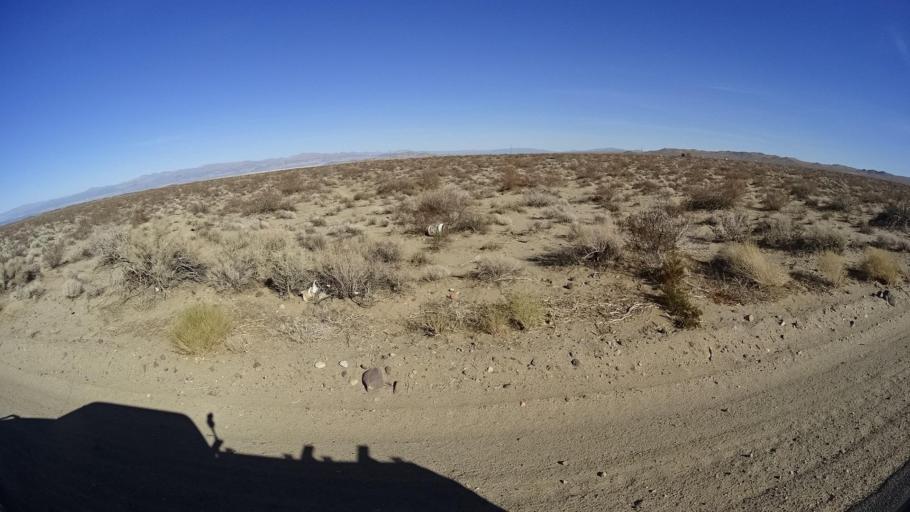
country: US
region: California
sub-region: Kern County
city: China Lake Acres
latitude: 35.5735
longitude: -117.7828
